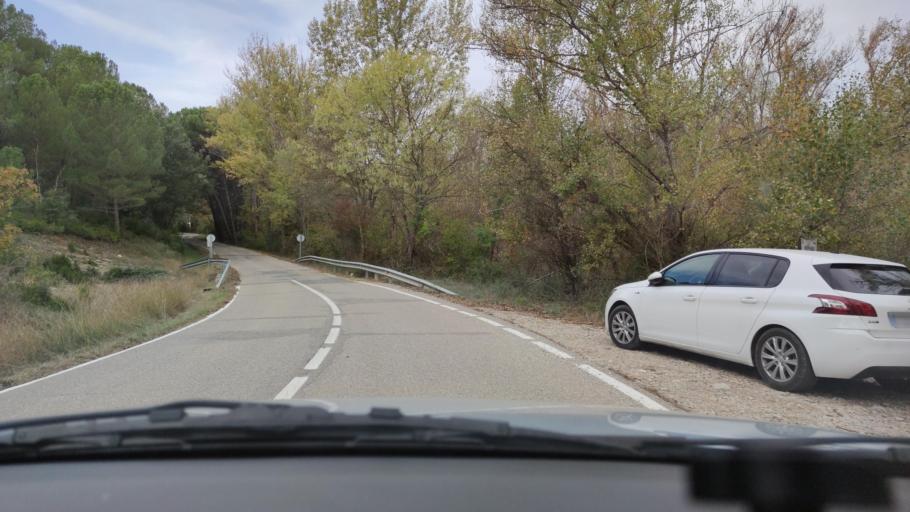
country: ES
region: Catalonia
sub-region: Provincia de Lleida
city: Llimiana
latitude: 42.0605
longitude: 0.8953
